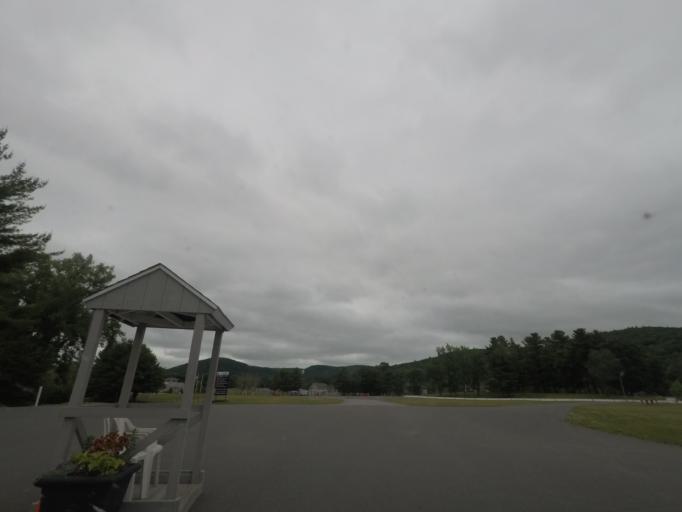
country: US
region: Connecticut
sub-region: Litchfield County
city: Canaan
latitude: 41.9276
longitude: -73.3855
